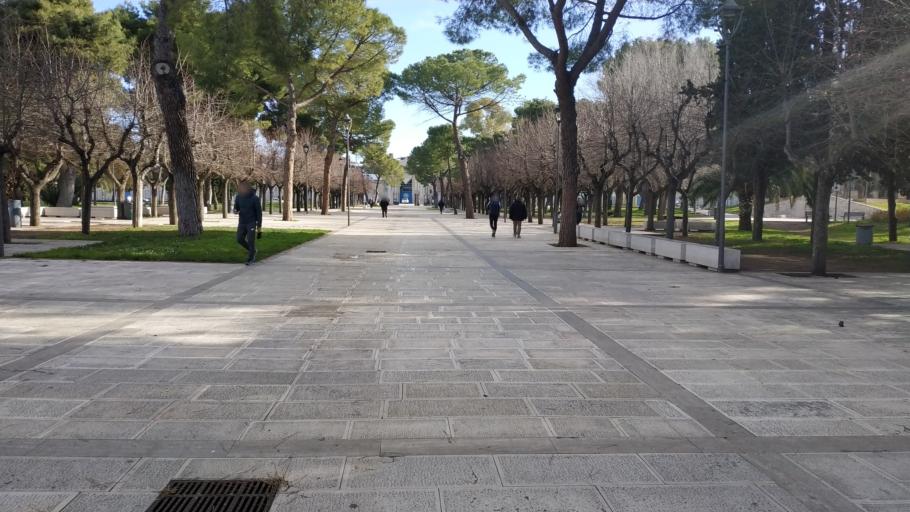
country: IT
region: Apulia
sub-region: Provincia di Barletta - Andria - Trani
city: Andria
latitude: 41.2319
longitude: 16.3069
